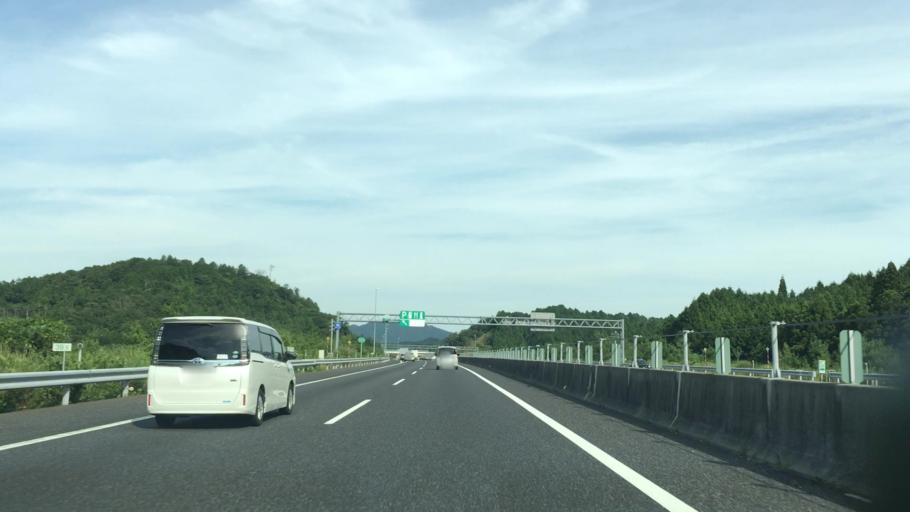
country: JP
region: Shiga Prefecture
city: Hino
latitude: 34.9182
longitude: 136.2806
